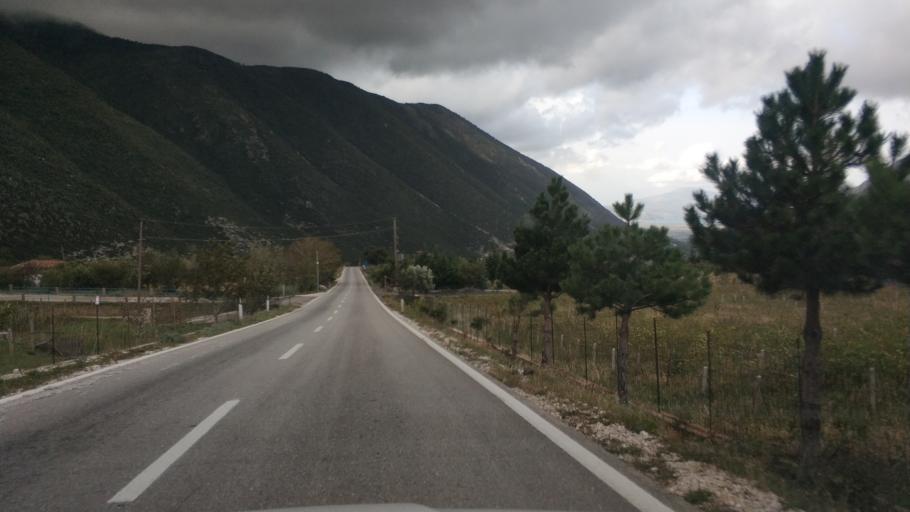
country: AL
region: Vlore
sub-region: Rrethi i Vlores
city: Brataj
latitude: 40.2306
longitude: 19.5704
